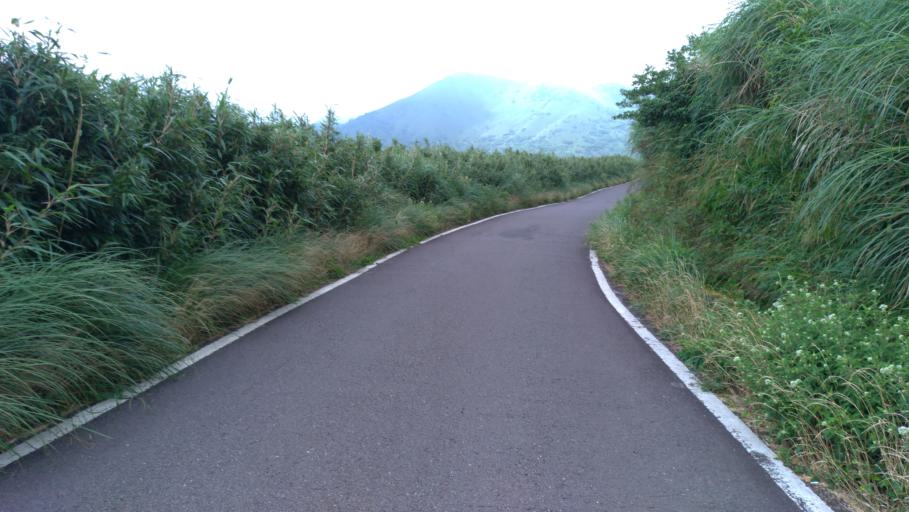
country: TW
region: Taipei
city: Taipei
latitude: 25.1810
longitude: 121.5224
